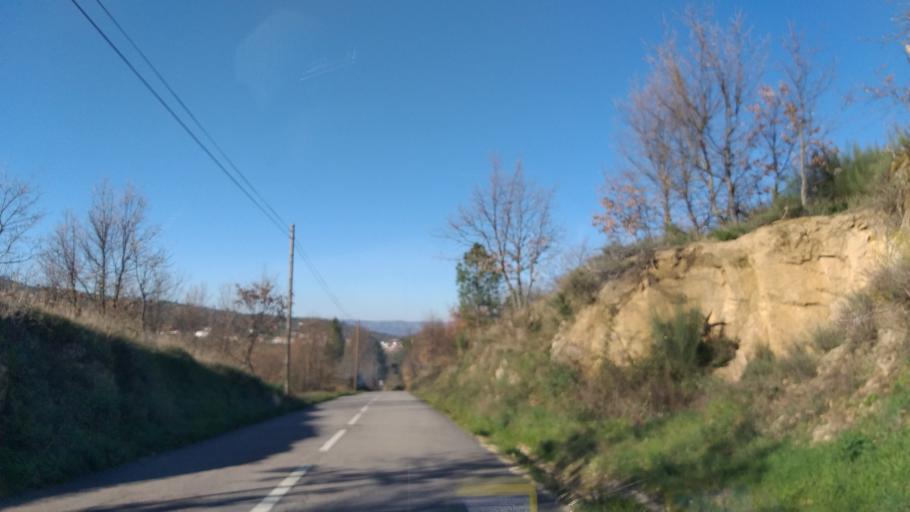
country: PT
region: Guarda
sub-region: Celorico da Beira
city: Celorico da Beira
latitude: 40.5911
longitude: -7.3623
